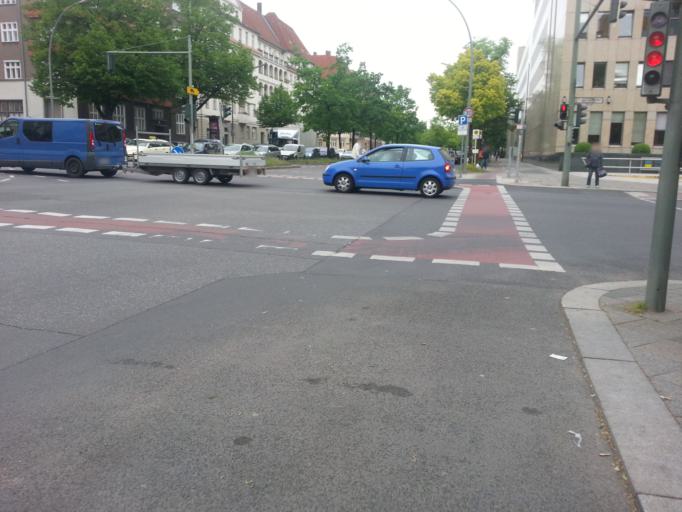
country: DE
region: Berlin
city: Charlottenburg Bezirk
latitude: 52.5128
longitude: 13.2817
